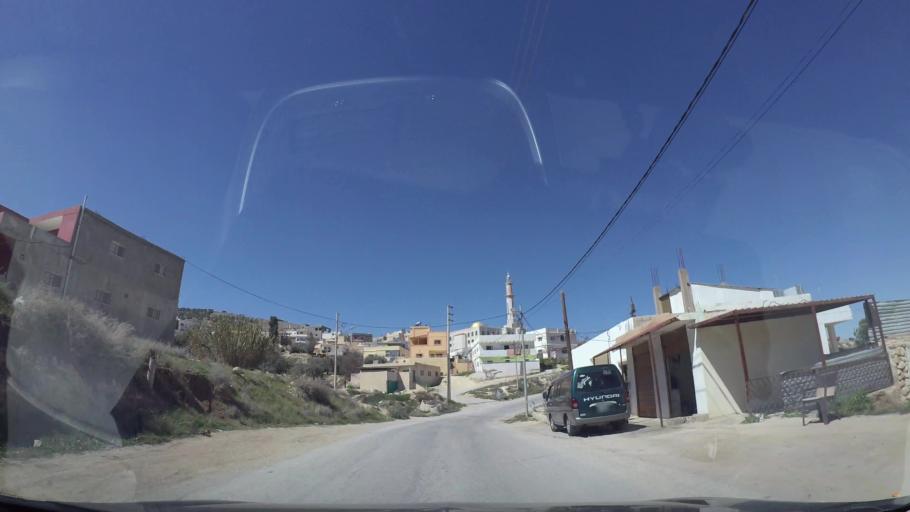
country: JO
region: Tafielah
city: At Tafilah
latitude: 30.8193
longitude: 35.5845
